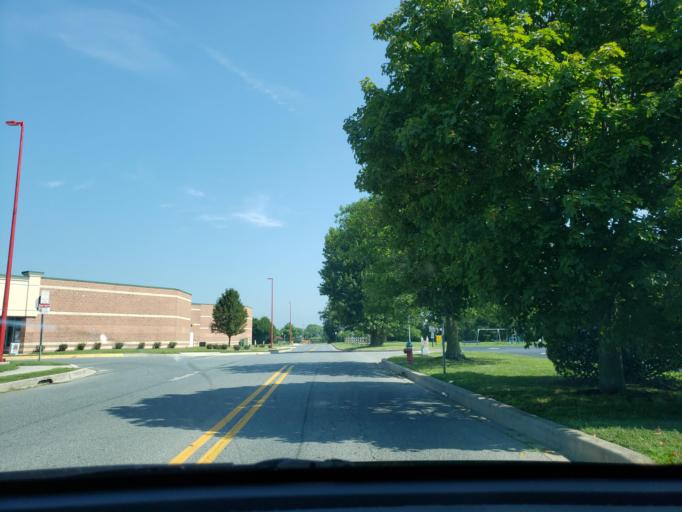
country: US
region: Delaware
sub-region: Kent County
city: Dover
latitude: 39.1579
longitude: -75.5081
